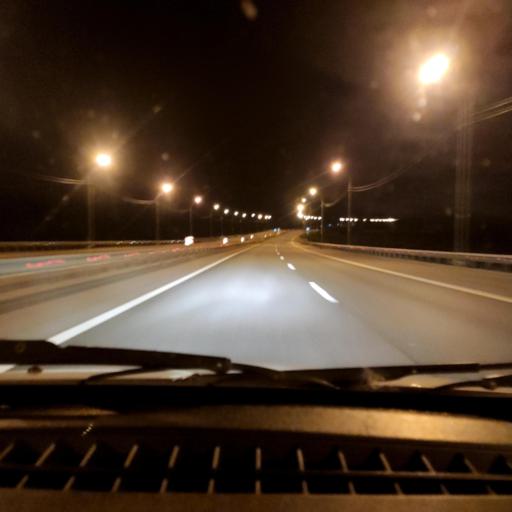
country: RU
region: Lipetsk
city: Zadonsk
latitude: 52.3402
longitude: 38.9641
